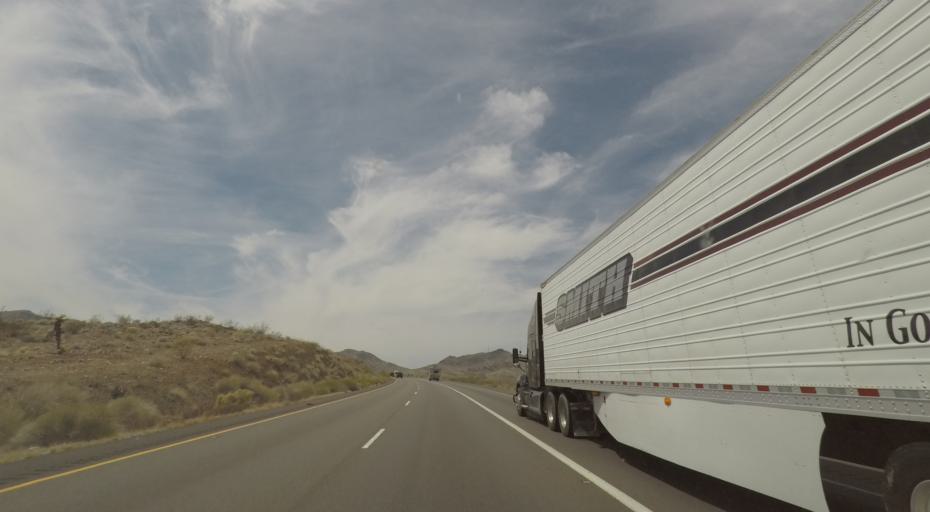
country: US
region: California
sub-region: San Bernardino County
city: Needles
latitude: 34.8704
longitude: -114.8304
